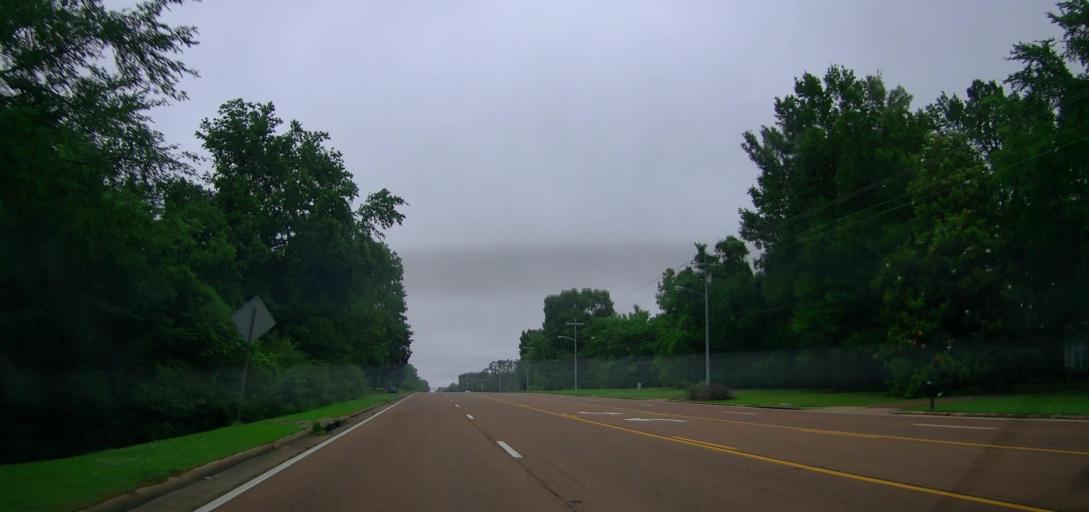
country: US
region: Mississippi
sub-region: De Soto County
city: Olive Branch
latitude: 34.9775
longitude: -89.8307
